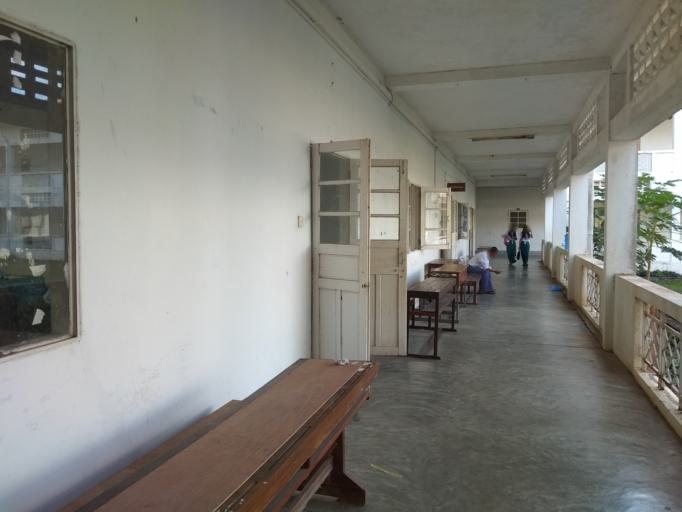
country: MM
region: Ayeyarwady
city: Maubin
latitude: 16.7004
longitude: 95.6577
